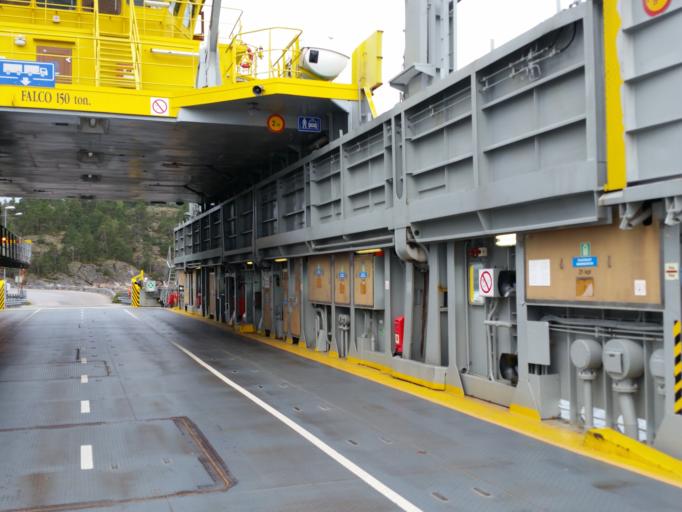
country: FI
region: Varsinais-Suomi
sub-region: Aboland-Turunmaa
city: Nagu
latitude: 60.2228
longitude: 22.0987
